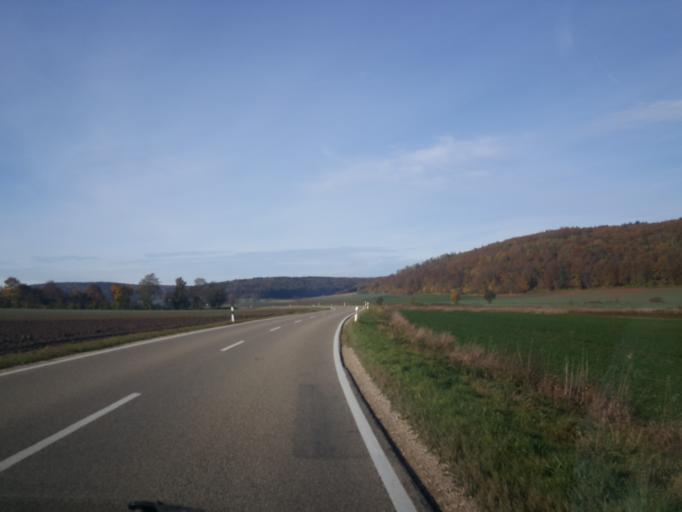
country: DE
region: Bavaria
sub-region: Upper Bavaria
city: Rennertshofen
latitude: 48.7912
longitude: 11.0976
